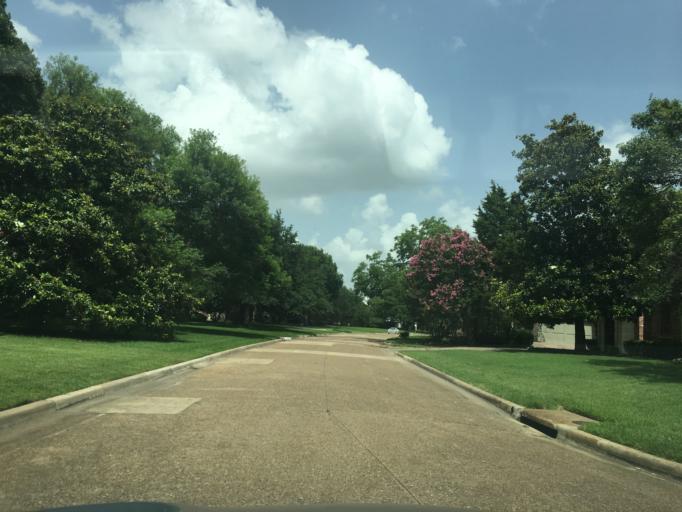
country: US
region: Texas
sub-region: Dallas County
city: University Park
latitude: 32.8901
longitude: -96.7981
